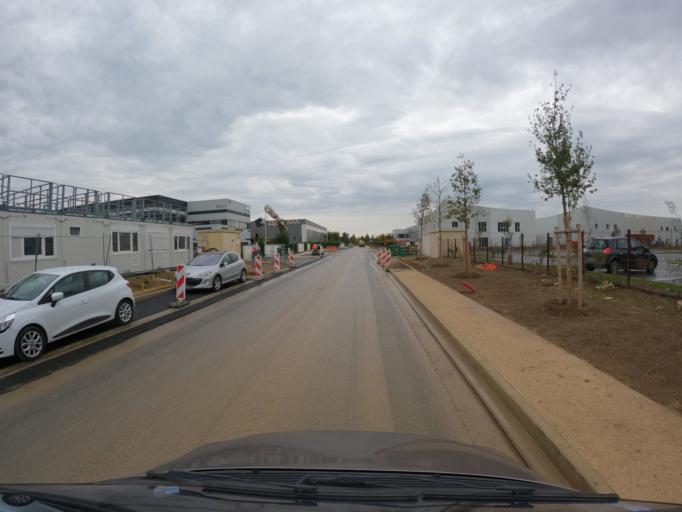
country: FR
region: Ile-de-France
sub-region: Departement de Seine-et-Marne
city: Serris
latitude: 48.8403
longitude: 2.7985
